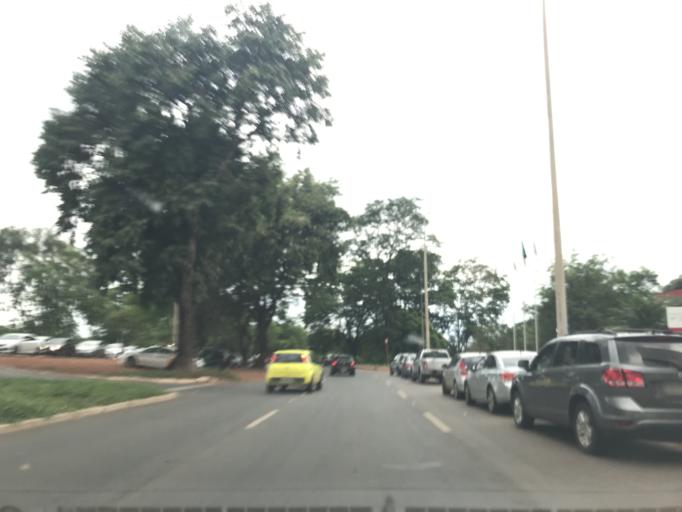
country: BR
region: Federal District
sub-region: Brasilia
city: Brasilia
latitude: -15.8031
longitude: -47.8801
